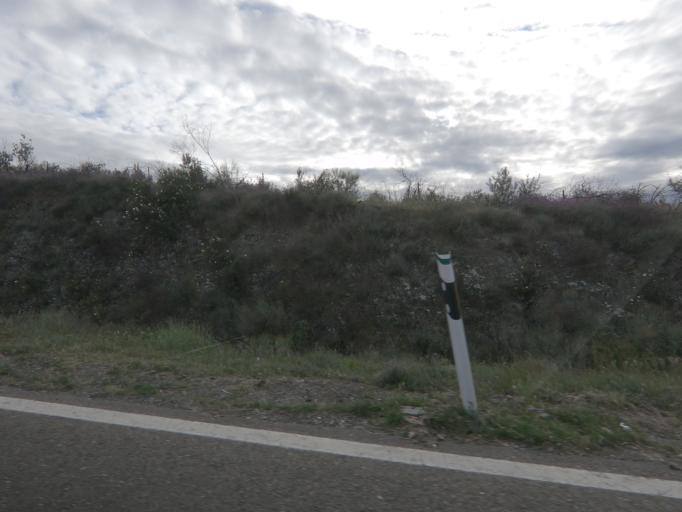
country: ES
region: Extremadura
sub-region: Provincia de Caceres
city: Coria
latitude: 39.9474
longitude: -6.5084
